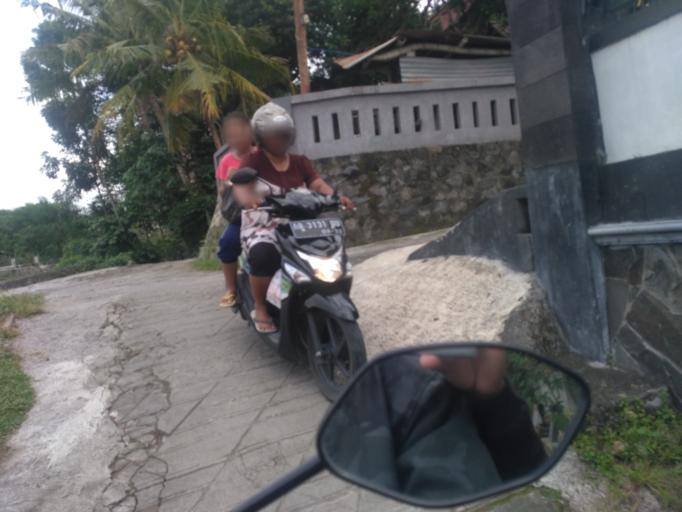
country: ID
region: Daerah Istimewa Yogyakarta
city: Yogyakarta
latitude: -7.7660
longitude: 110.3517
